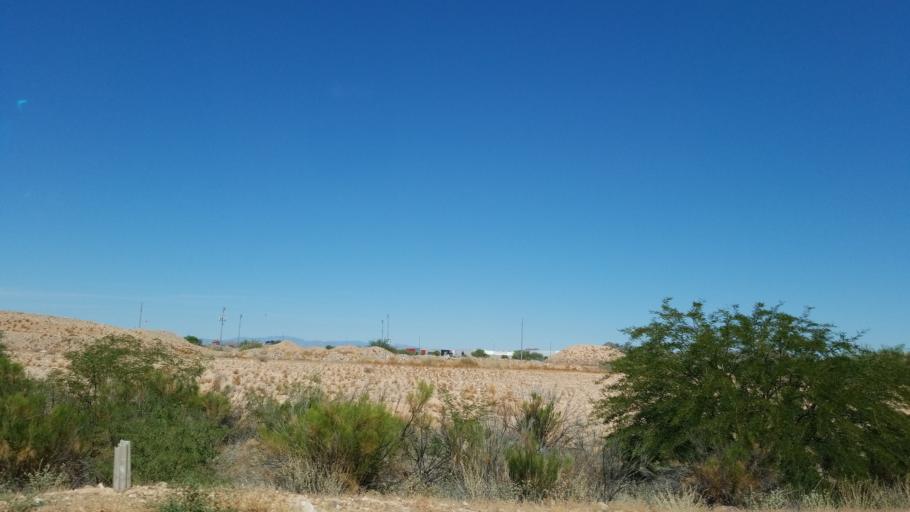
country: US
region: Arizona
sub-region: Maricopa County
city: Sun City West
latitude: 33.6789
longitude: -112.2669
